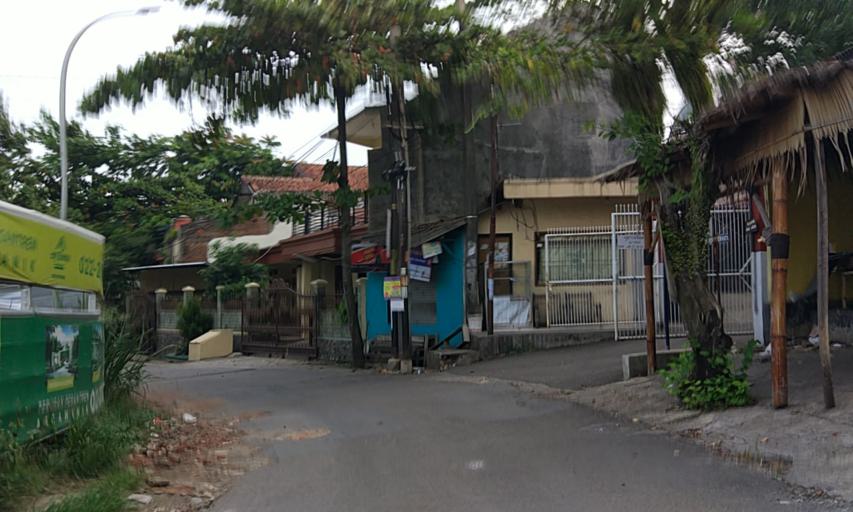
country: ID
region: West Java
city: Bandung
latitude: -6.9125
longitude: 107.6815
